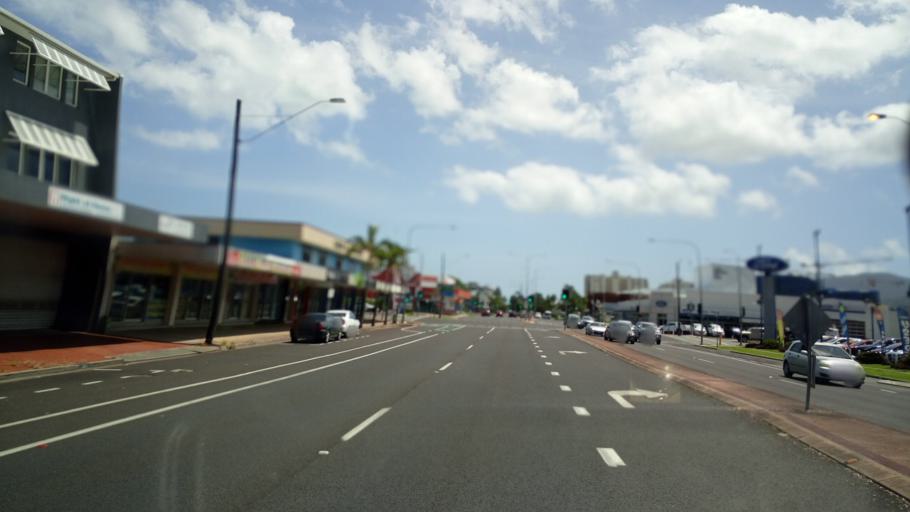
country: AU
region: Queensland
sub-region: Cairns
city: Cairns
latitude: -16.9217
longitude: 145.7690
